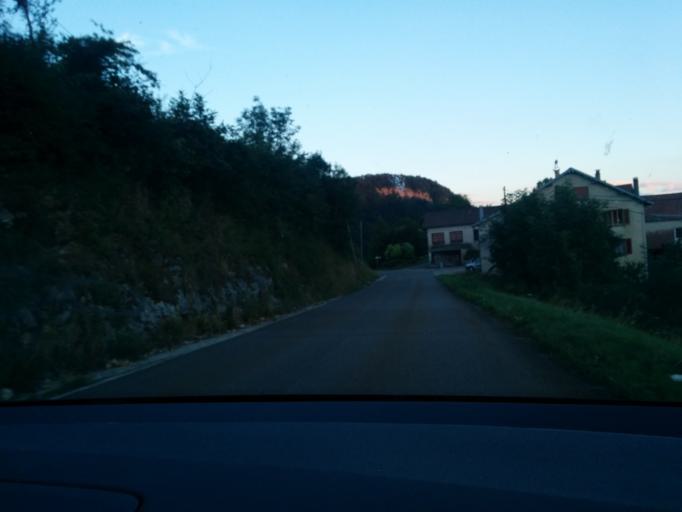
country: FR
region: Franche-Comte
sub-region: Departement du Jura
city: Saint-Lupicin
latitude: 46.4595
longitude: 5.7964
